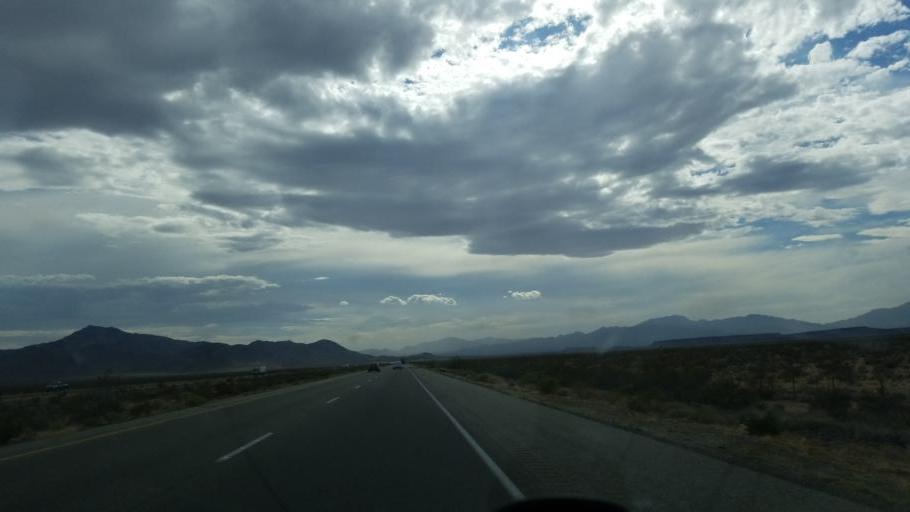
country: US
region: California
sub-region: San Bernardino County
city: Needles
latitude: 34.8057
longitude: -115.2669
